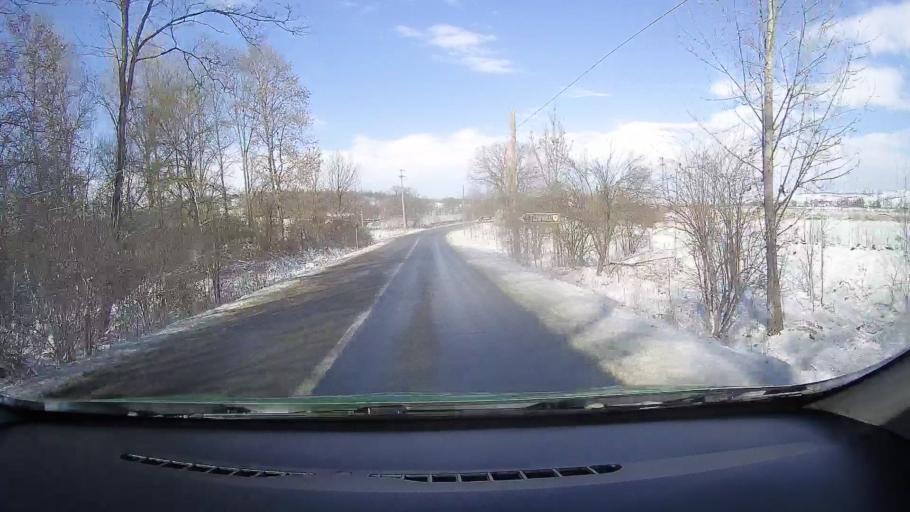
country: RO
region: Sibiu
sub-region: Comuna Nocrich
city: Nocrich
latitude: 45.8701
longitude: 24.4516
